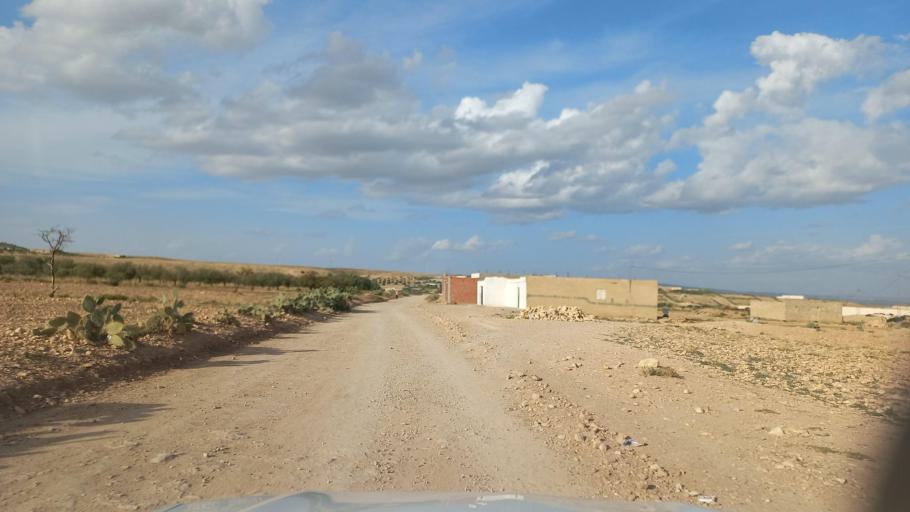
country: TN
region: Al Qasrayn
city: Sbiba
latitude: 35.4481
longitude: 9.0818
